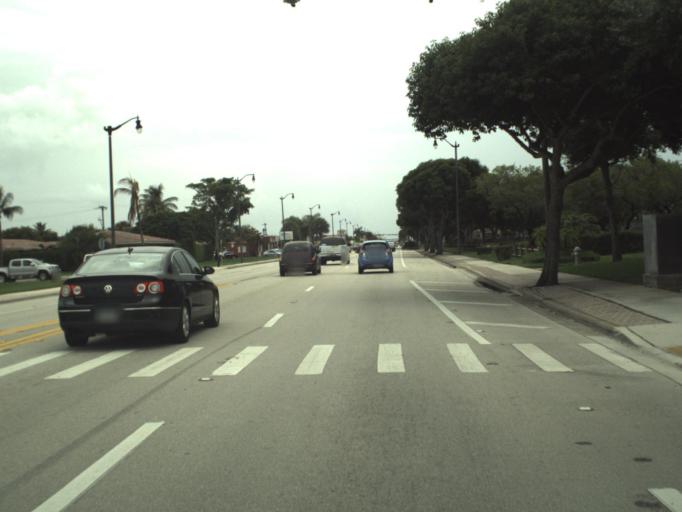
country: US
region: Florida
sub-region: Palm Beach County
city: Lake Clarke Shores
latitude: 26.6734
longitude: -80.0550
